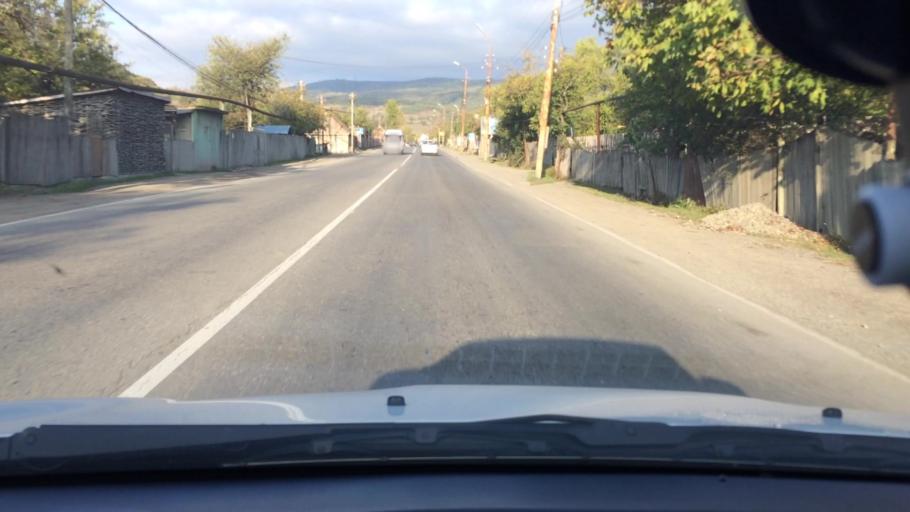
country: GE
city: Surami
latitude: 42.0274
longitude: 43.5403
